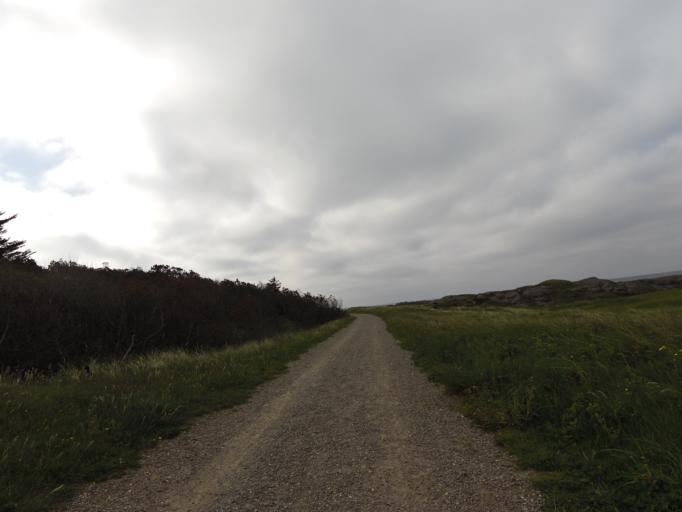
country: NO
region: Rogaland
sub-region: Ha
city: Vigrestad
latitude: 58.5274
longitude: 5.7755
